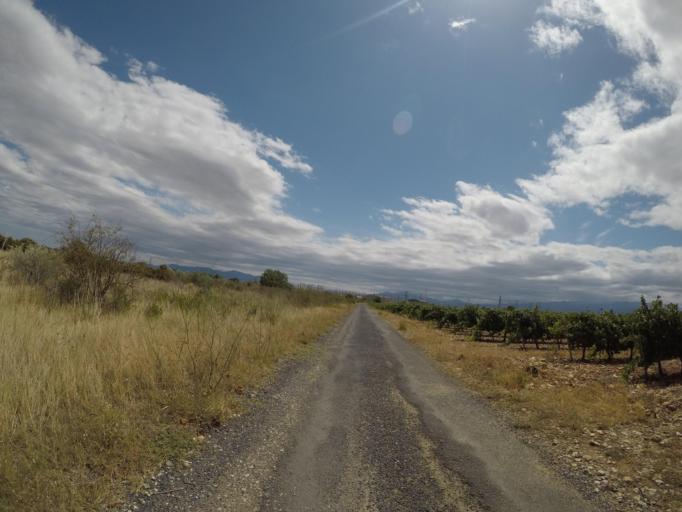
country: FR
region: Languedoc-Roussillon
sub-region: Departement des Pyrenees-Orientales
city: Baixas
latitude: 42.7388
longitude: 2.8030
